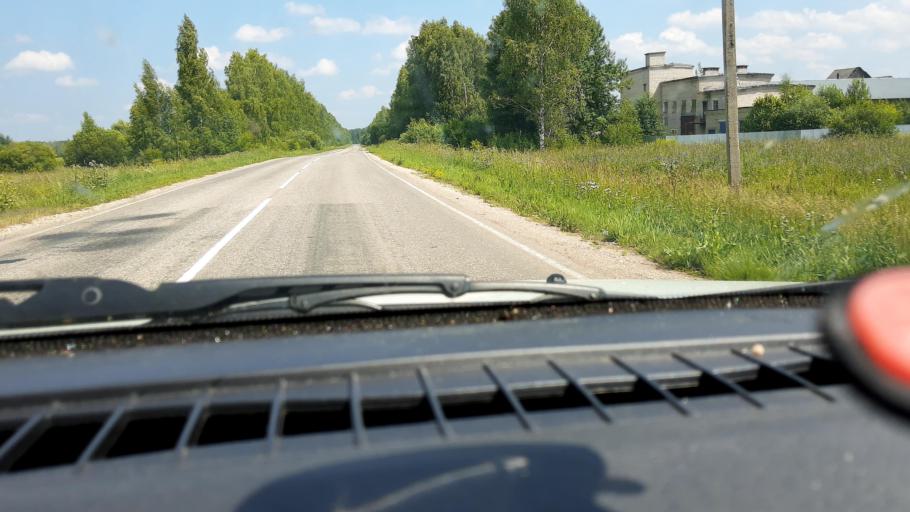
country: RU
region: Nizjnij Novgorod
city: Sharanga
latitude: 57.1301
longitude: 46.5118
